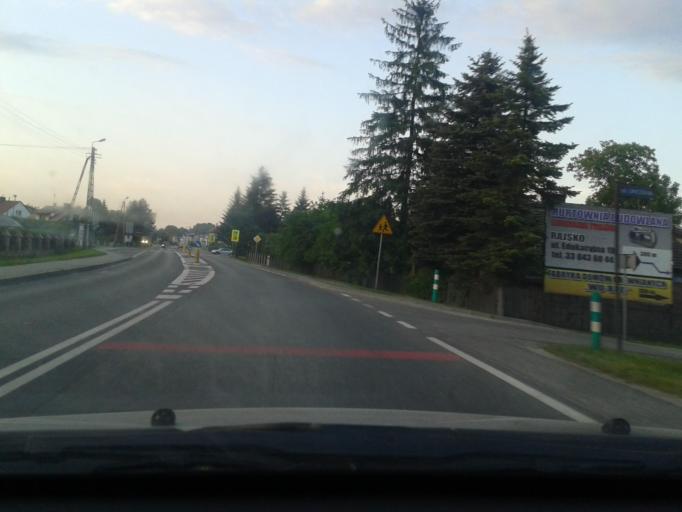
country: PL
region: Lesser Poland Voivodeship
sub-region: Powiat oswiecimski
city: Rajsko
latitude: 50.0090
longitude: 19.1918
